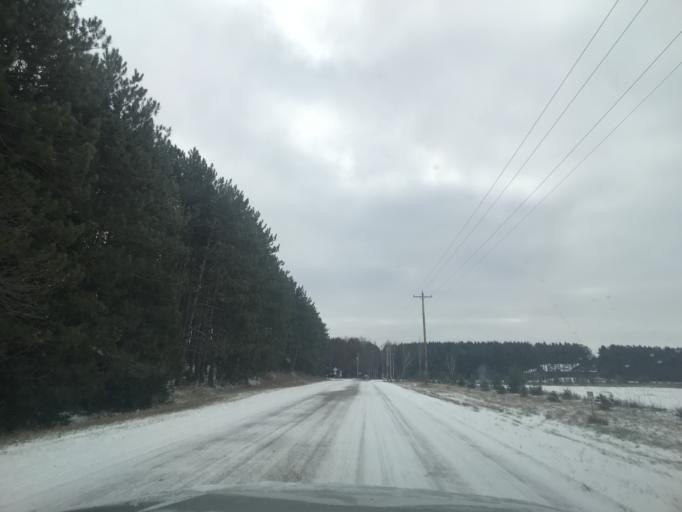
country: US
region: Wisconsin
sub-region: Brown County
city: Suamico
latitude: 44.6932
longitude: -88.1008
